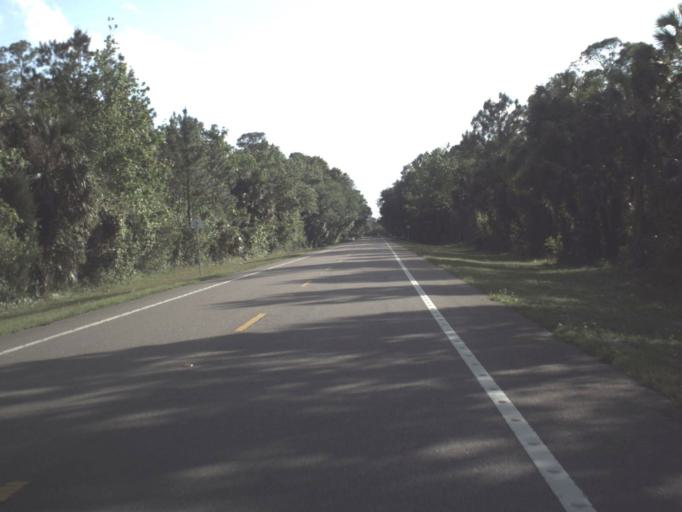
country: US
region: Florida
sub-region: Flagler County
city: Bunnell
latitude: 29.4485
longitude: -81.2738
